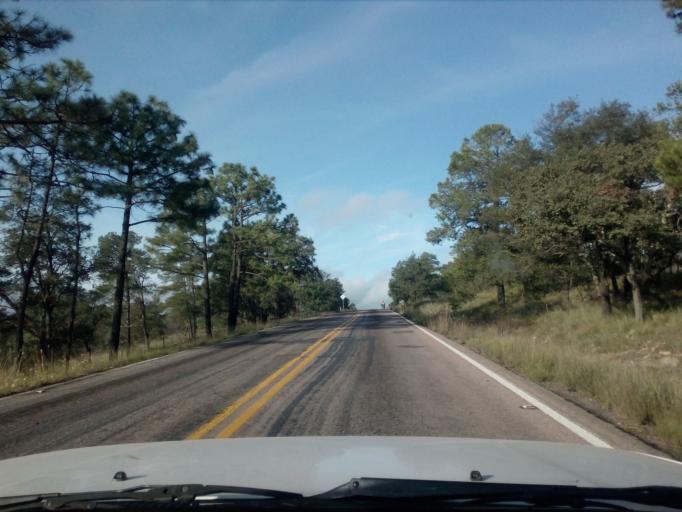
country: MX
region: Durango
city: Victoria de Durango
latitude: 23.9326
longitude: -104.9152
